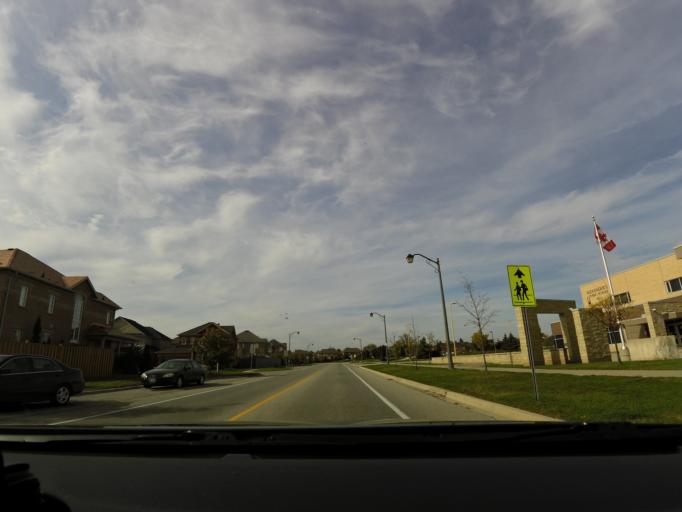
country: CA
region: Ontario
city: Burlington
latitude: 43.4054
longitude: -79.7856
